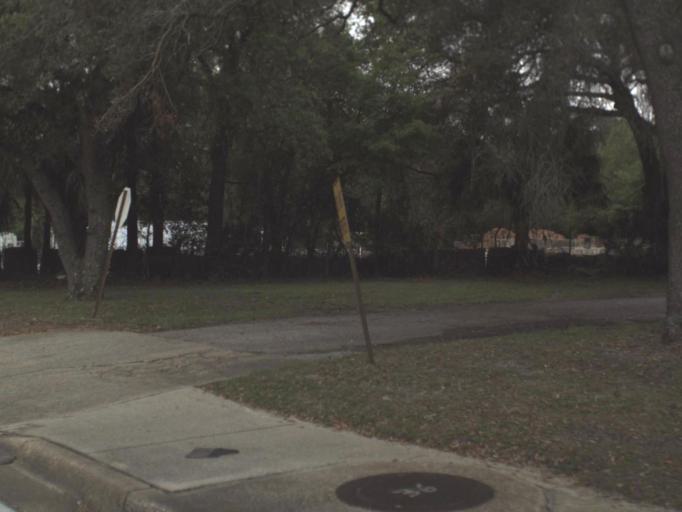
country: US
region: Florida
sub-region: Okaloosa County
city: Wright
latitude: 30.4581
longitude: -86.6359
